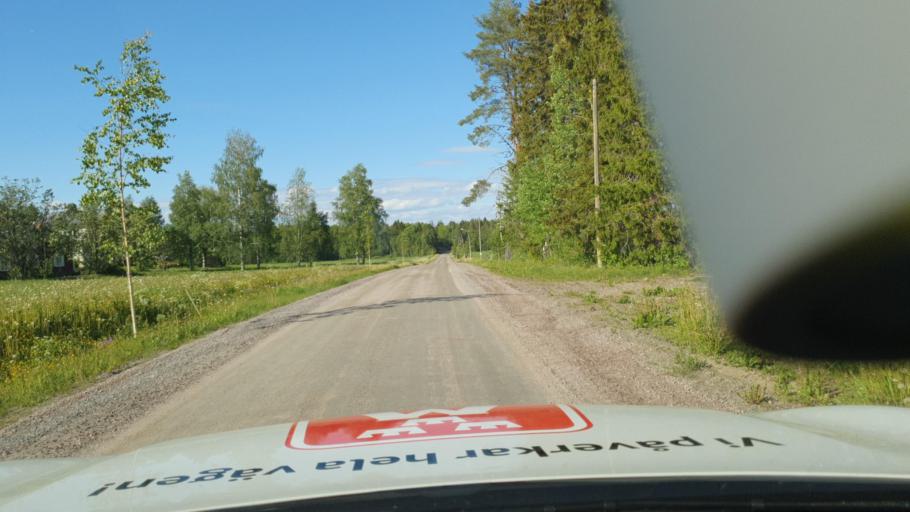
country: SE
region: Vaesterbotten
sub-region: Vannas Kommun
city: Vaennaes
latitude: 63.8296
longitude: 19.6289
